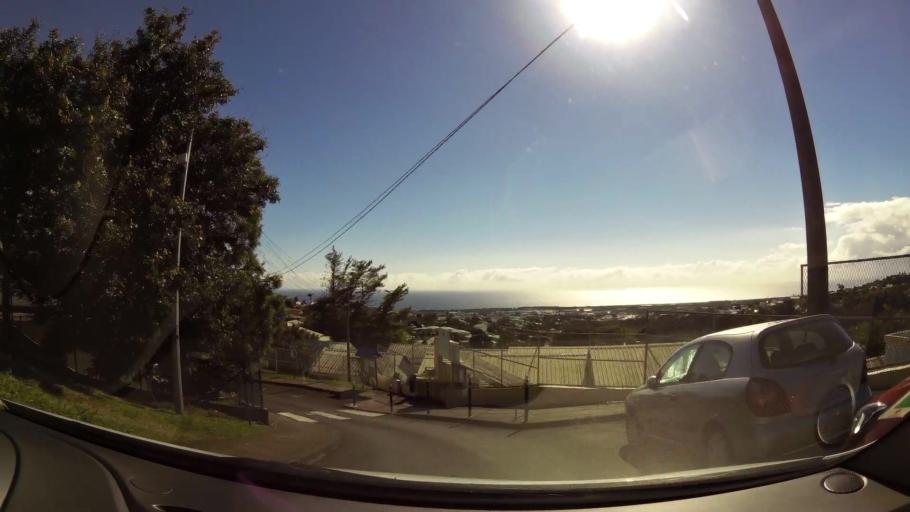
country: RE
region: Reunion
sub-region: Reunion
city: Saint-Denis
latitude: -20.9169
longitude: 55.4860
